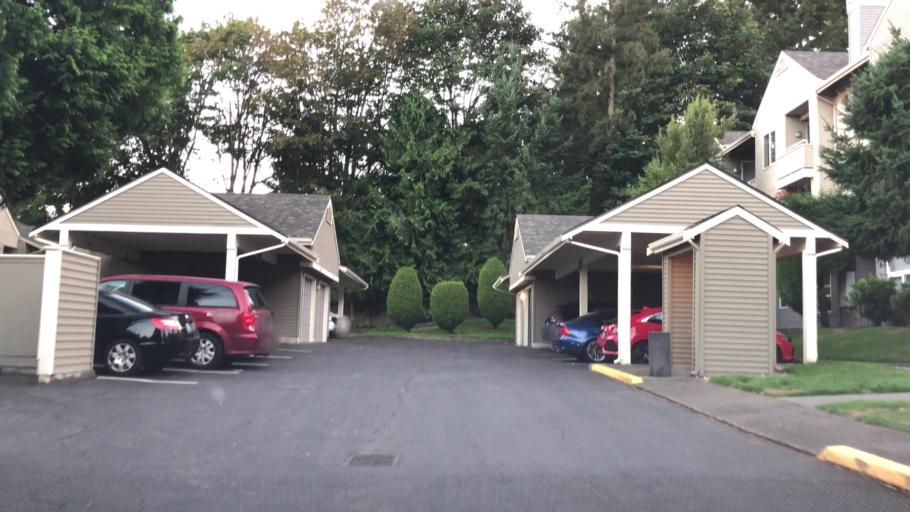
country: US
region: Washington
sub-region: King County
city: Redmond
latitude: 47.6823
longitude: -122.1044
